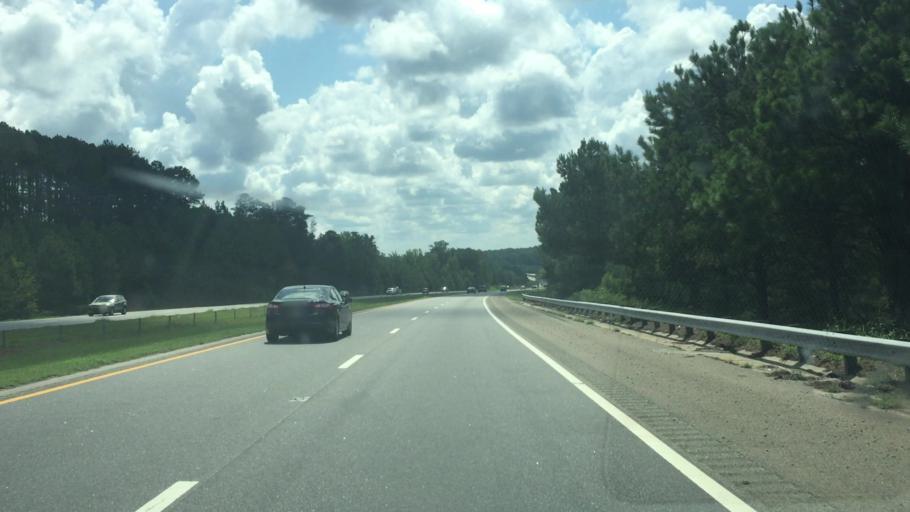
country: US
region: North Carolina
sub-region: Richmond County
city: Cordova
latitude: 34.9286
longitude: -79.8237
